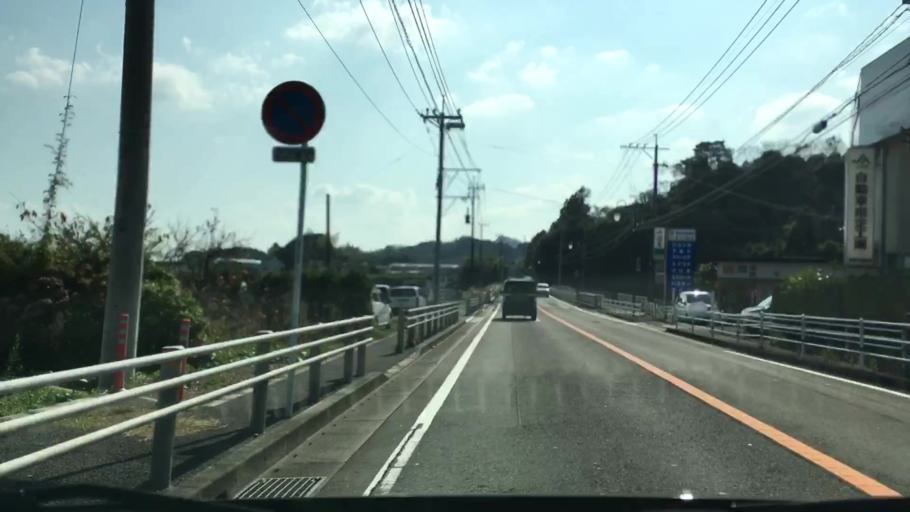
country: JP
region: Nagasaki
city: Togitsu
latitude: 32.9445
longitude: 129.7822
